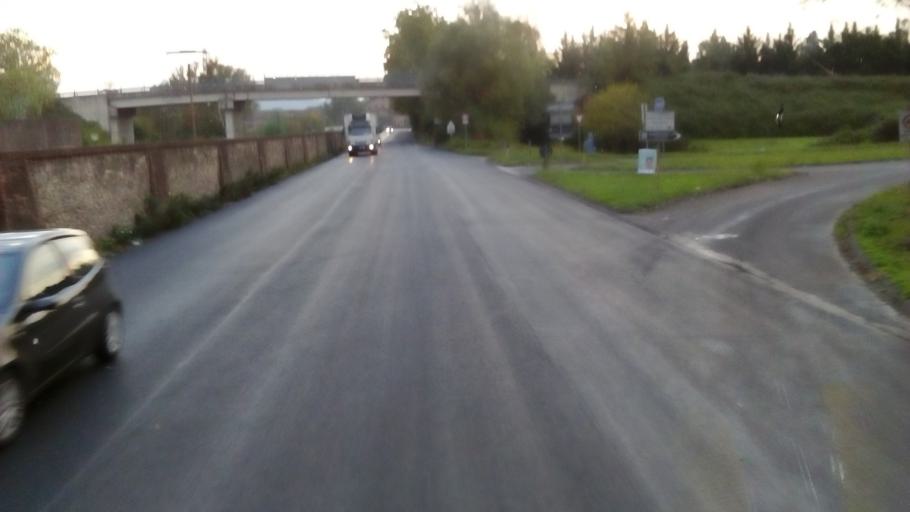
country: IT
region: Tuscany
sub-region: Province of Florence
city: Castelfiorentino
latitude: 43.6483
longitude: 10.9516
